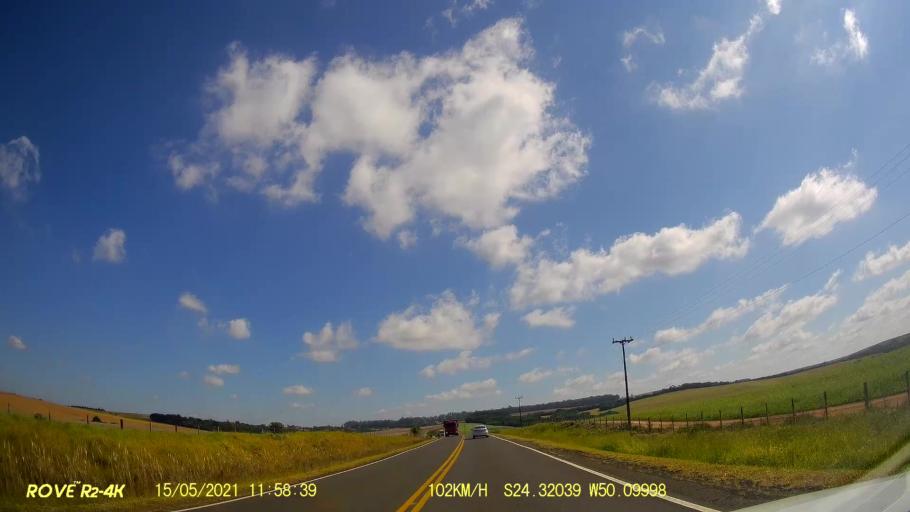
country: BR
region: Parana
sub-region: Pirai Do Sul
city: Pirai do Sul
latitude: -24.3211
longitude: -50.1000
